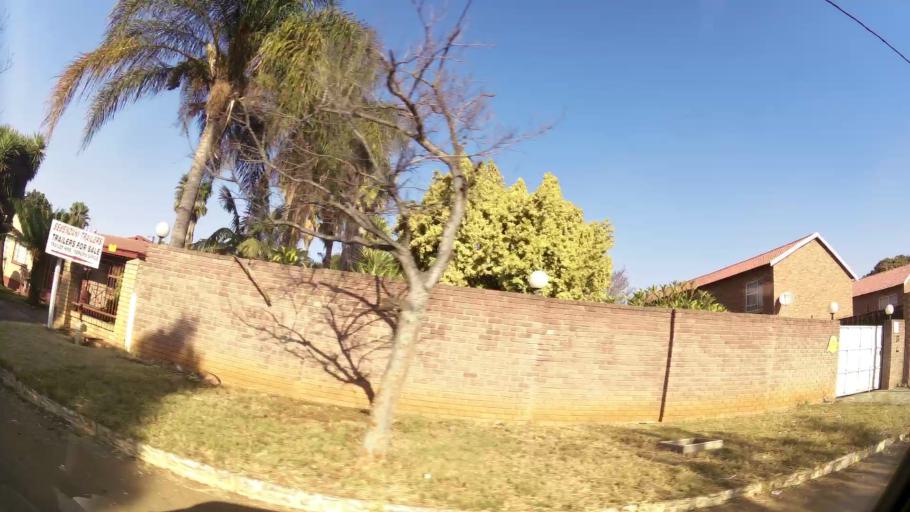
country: ZA
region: North-West
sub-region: Bojanala Platinum District Municipality
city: Rustenburg
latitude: -25.6539
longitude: 27.2469
